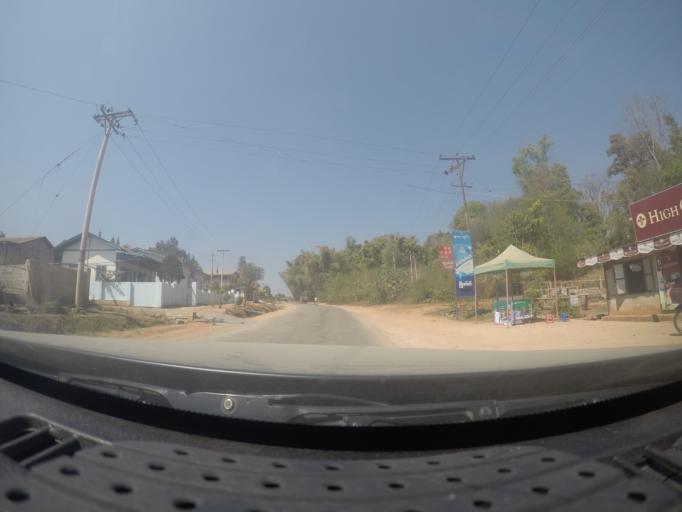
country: MM
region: Shan
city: Taunggyi
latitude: 20.7899
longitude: 96.6486
